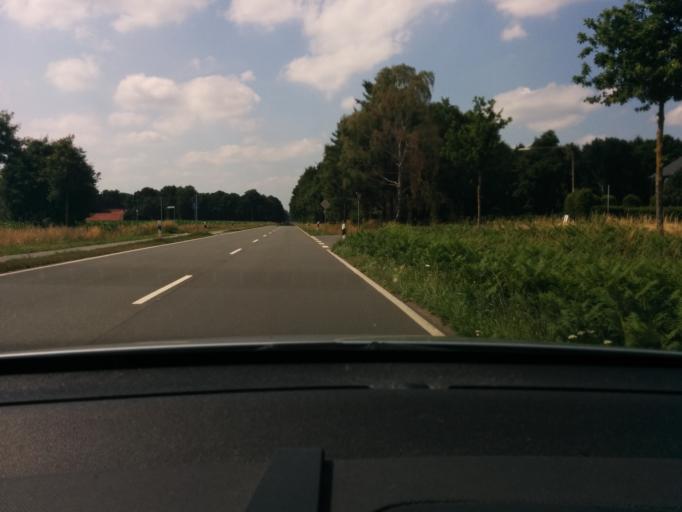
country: DE
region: North Rhine-Westphalia
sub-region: Regierungsbezirk Munster
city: Wettringen
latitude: 52.1844
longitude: 7.2664
